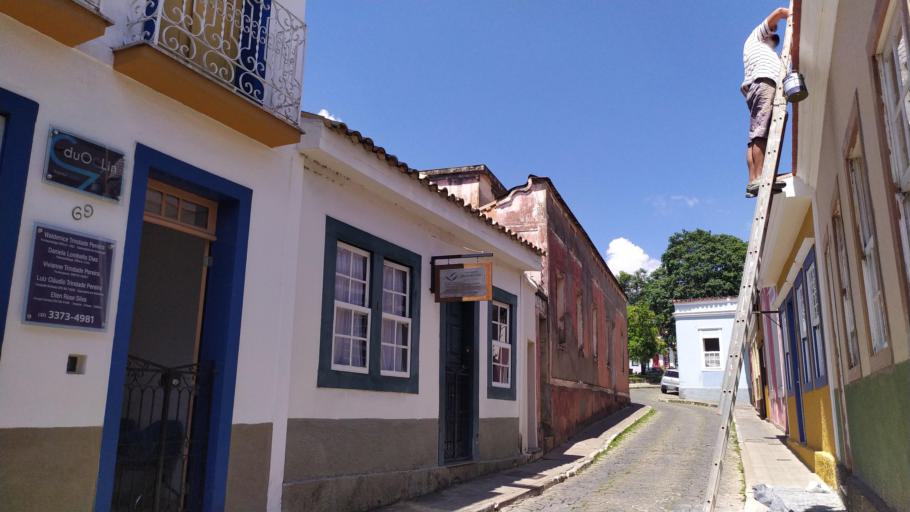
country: BR
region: Minas Gerais
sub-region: Sao Joao Del Rei
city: Sao Joao del Rei
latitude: -21.1337
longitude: -44.2612
